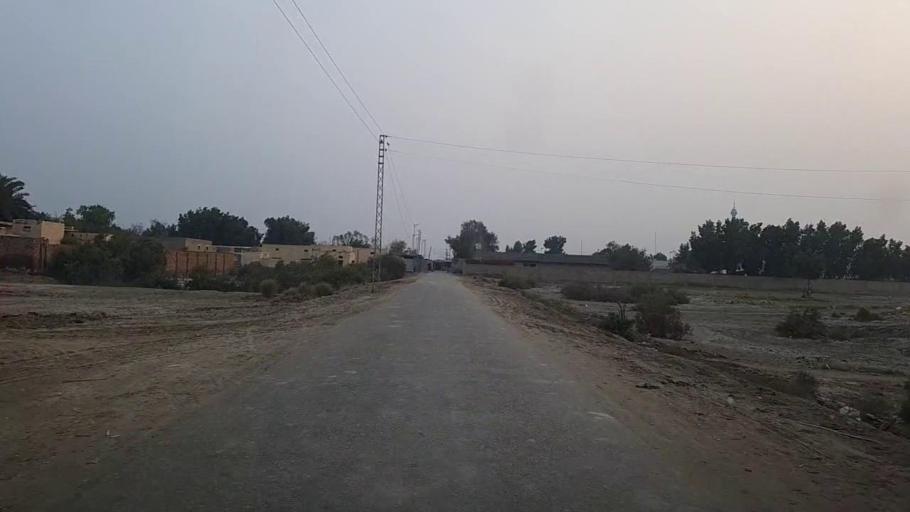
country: PK
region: Sindh
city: Kandiari
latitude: 26.9277
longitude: 68.5008
